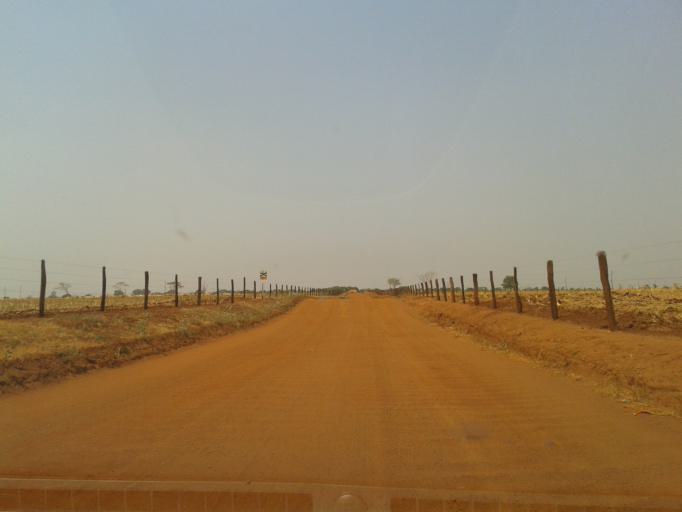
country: BR
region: Minas Gerais
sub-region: Centralina
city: Centralina
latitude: -18.7157
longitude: -49.2172
